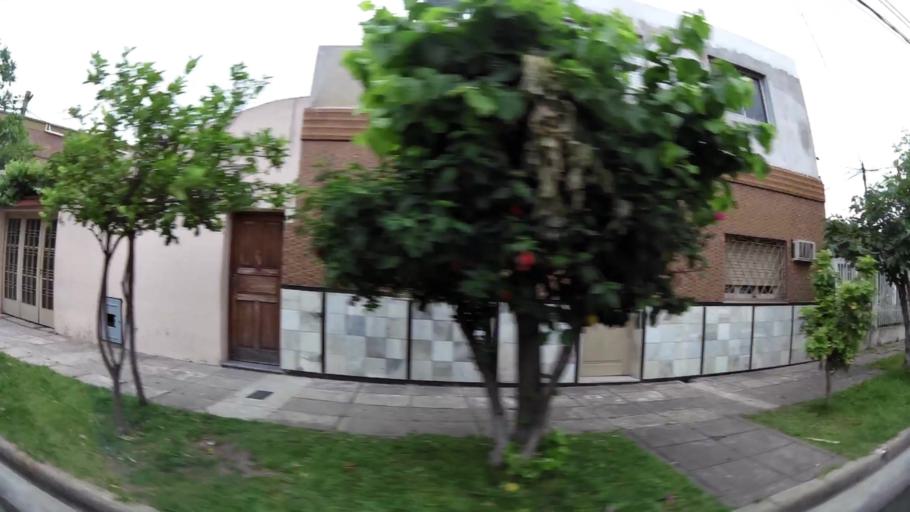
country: AR
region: Buenos Aires F.D.
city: Villa Lugano
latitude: -34.7076
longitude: -58.5100
